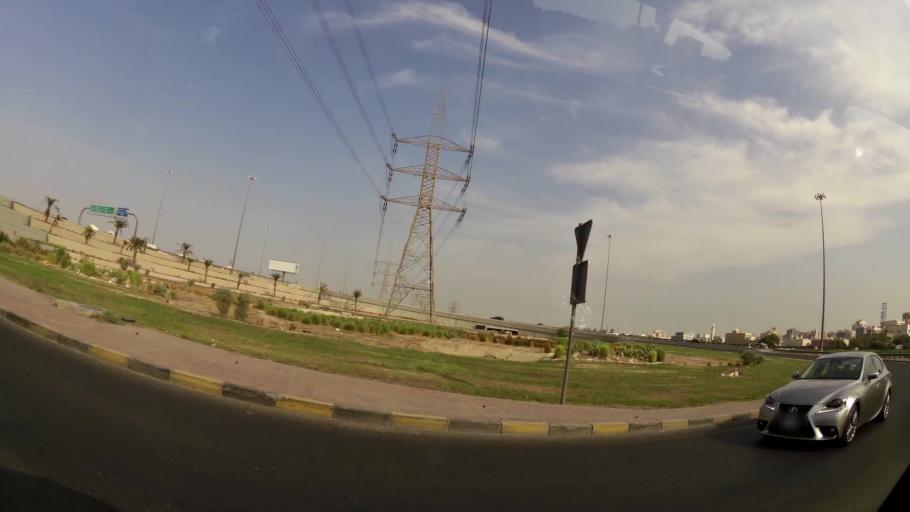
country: KW
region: Al Farwaniyah
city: Al Farwaniyah
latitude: 29.3019
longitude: 47.9639
